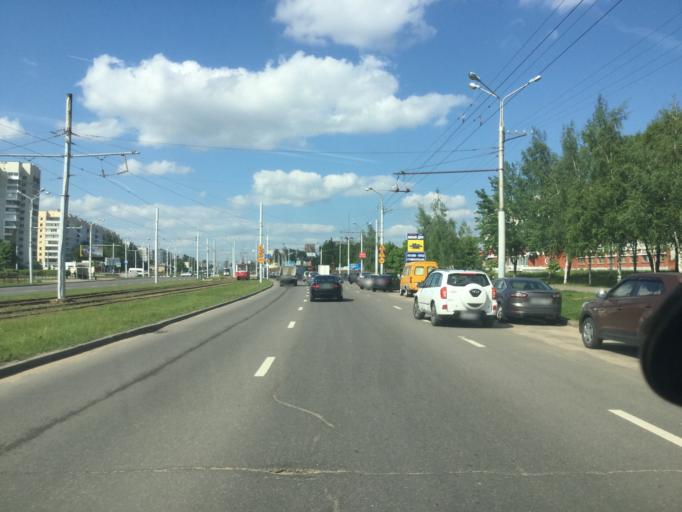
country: BY
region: Vitebsk
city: Vitebsk
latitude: 55.1661
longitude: 30.2407
